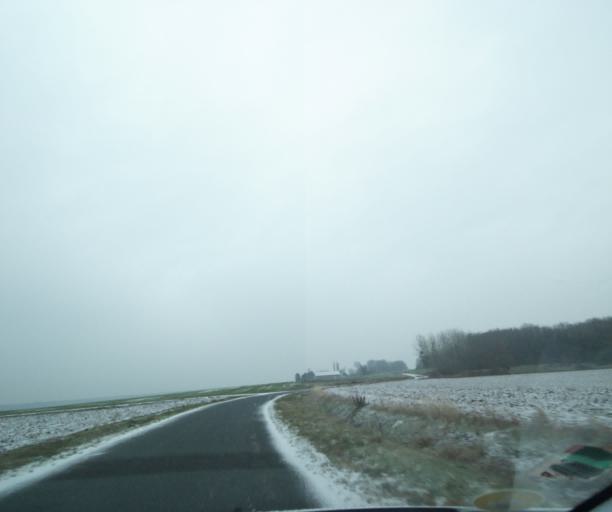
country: FR
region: Champagne-Ardenne
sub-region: Departement de la Haute-Marne
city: Chevillon
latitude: 48.4894
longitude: 5.0576
